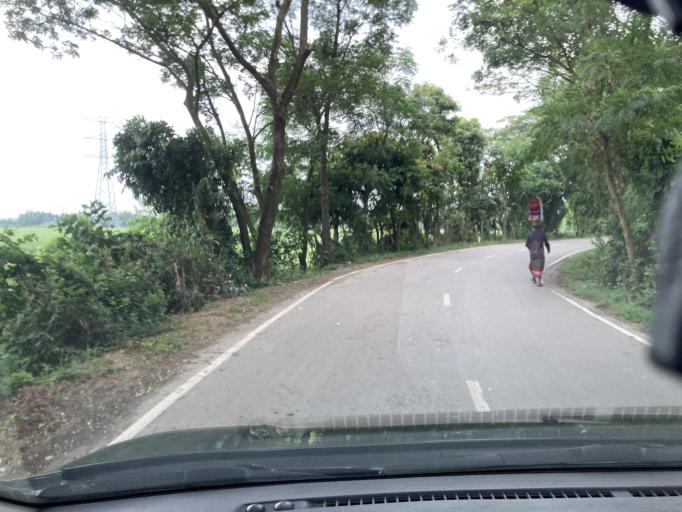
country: BD
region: Dhaka
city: Azimpur
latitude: 23.7786
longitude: 90.2075
